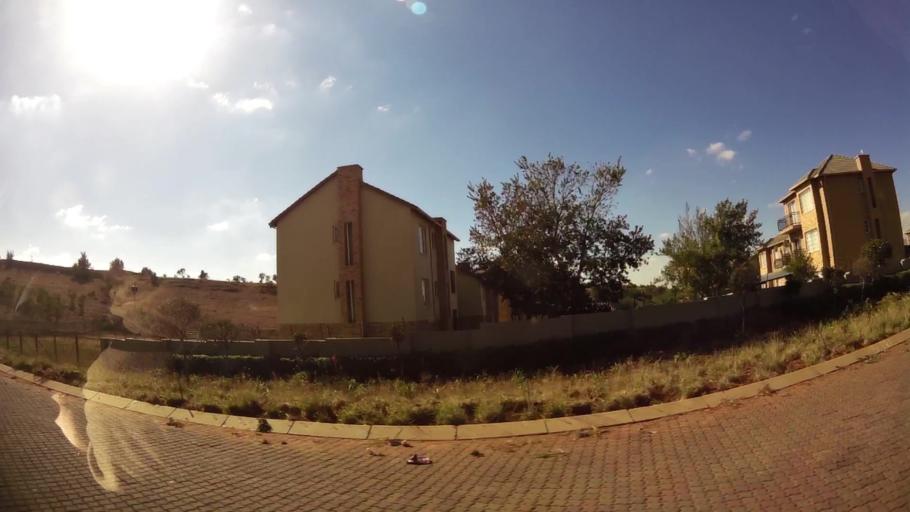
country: ZA
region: Gauteng
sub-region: West Rand District Municipality
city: Krugersdorp
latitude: -26.0854
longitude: 27.8150
